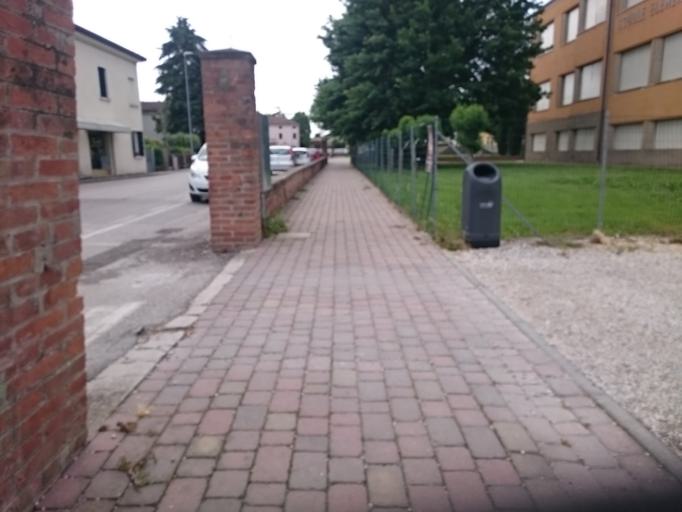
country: IT
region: Veneto
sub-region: Provincia di Padova
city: Megliadino San Vitale
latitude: 45.1939
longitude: 11.5259
